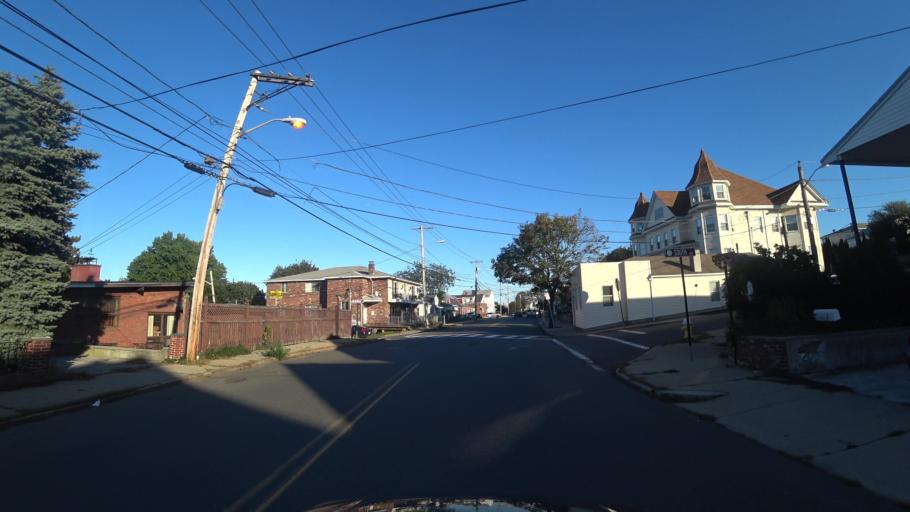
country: US
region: Massachusetts
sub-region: Suffolk County
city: Revere
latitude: 42.4202
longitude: -71.0145
